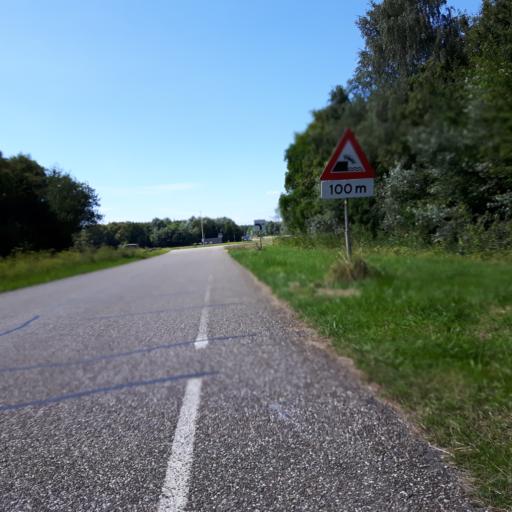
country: NL
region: North Brabant
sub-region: Gemeente Woensdrecht
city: Woensdrecht
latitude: 51.4299
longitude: 4.2370
